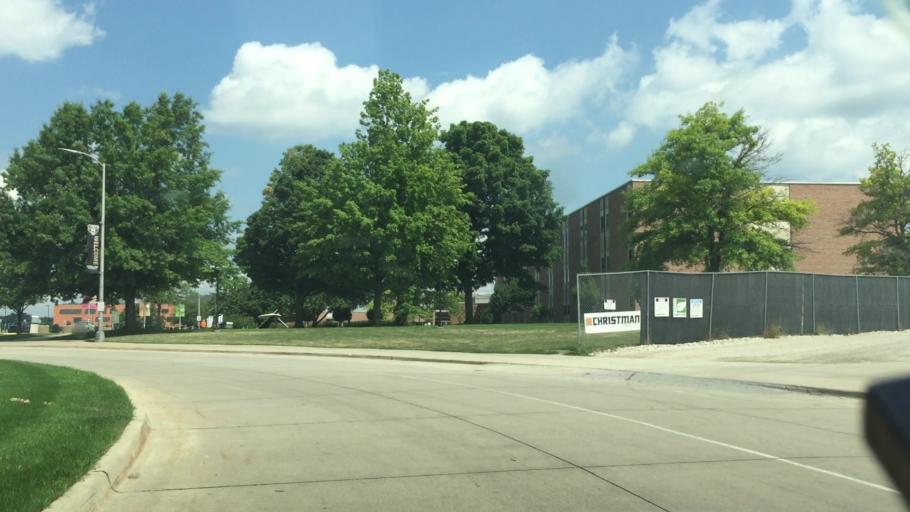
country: US
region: Michigan
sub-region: Oakland County
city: Auburn Hills
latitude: 42.6727
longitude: -83.2182
